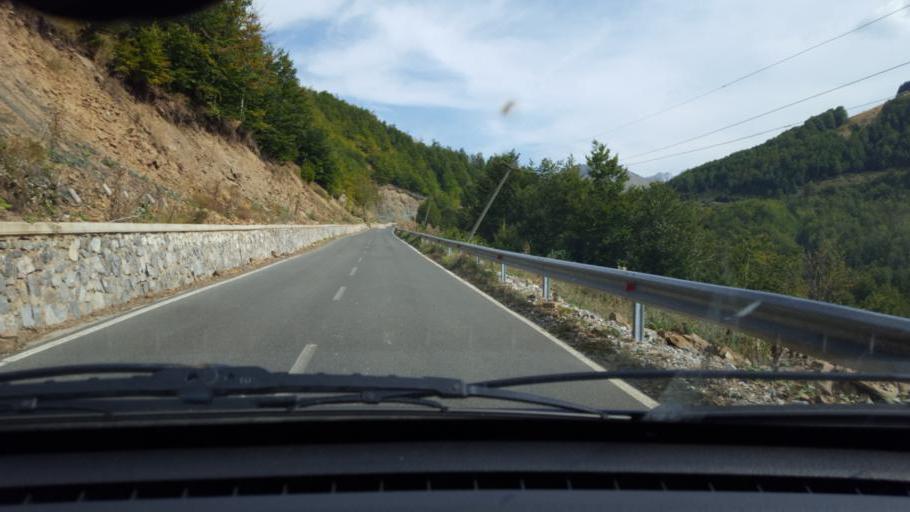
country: AL
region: Kukes
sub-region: Rrethi i Tropojes
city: Valbone
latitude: 42.5348
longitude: 19.7100
